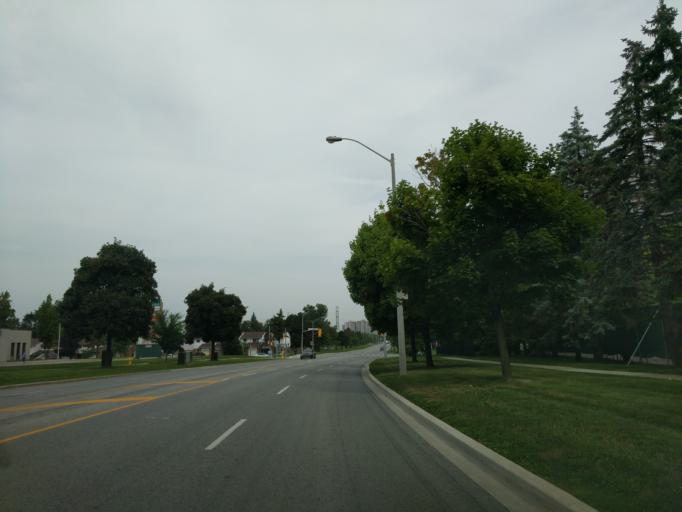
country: CA
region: Ontario
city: Scarborough
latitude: 43.8004
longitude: -79.3181
